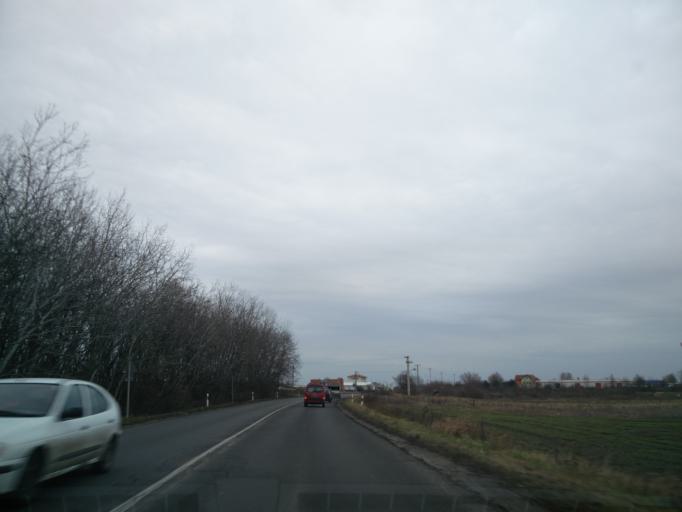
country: HU
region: Pest
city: Vecses
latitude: 47.3918
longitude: 19.3157
